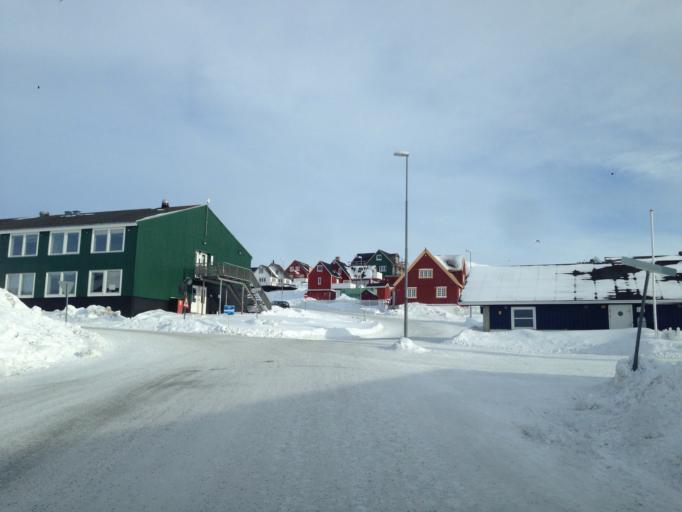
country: GL
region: Sermersooq
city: Nuuk
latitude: 64.1802
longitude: -51.7397
